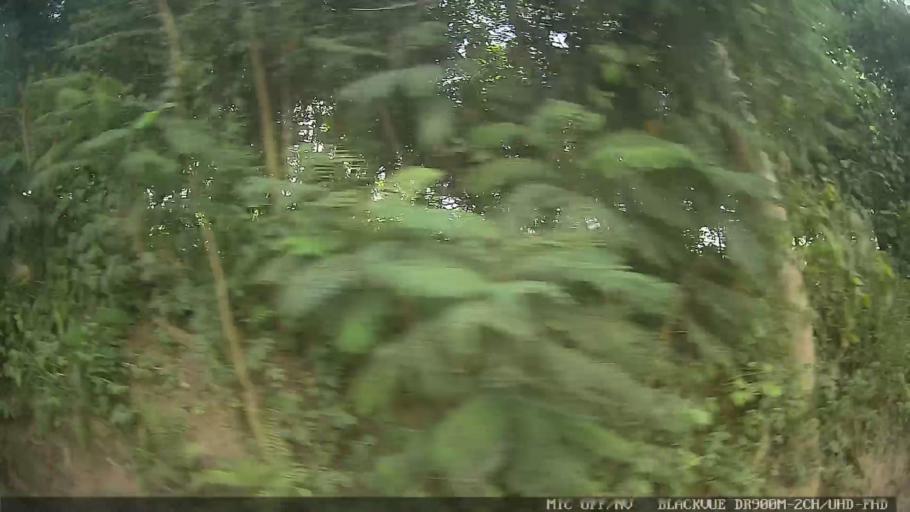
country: BR
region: Sao Paulo
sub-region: Bom Jesus Dos Perdoes
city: Bom Jesus dos Perdoes
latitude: -23.1276
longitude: -46.4987
